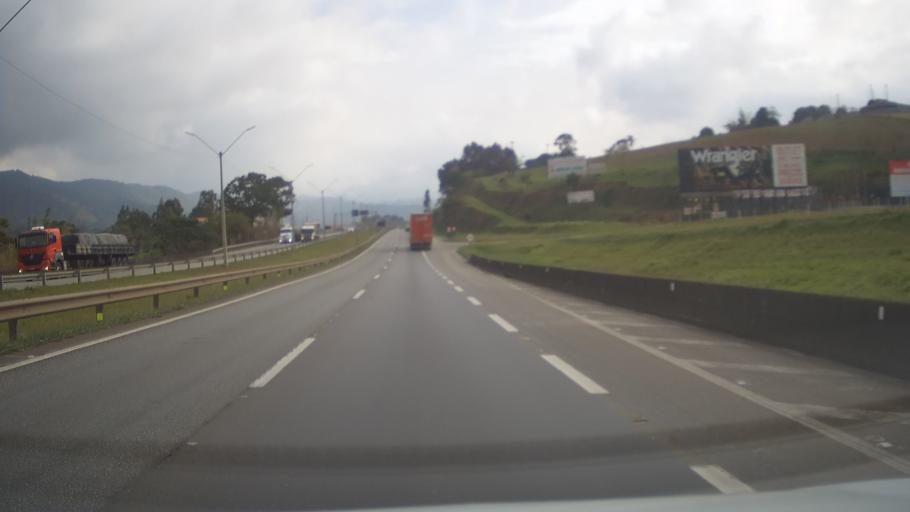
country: BR
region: Minas Gerais
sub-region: Extrema
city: Extrema
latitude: -22.9041
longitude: -46.4218
